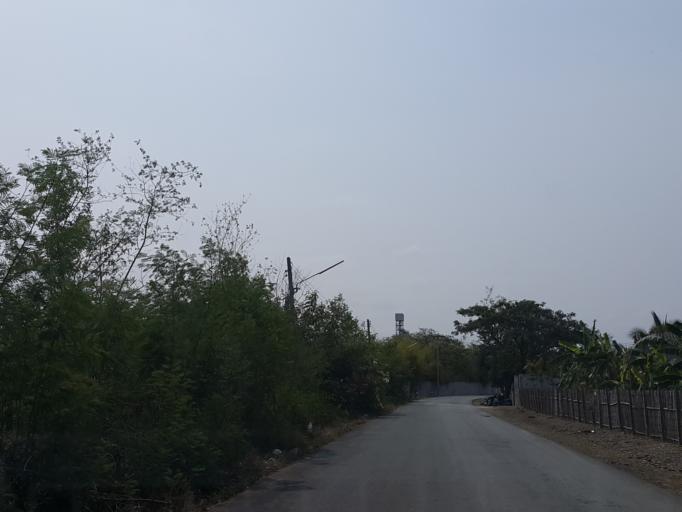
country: TH
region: Lamphun
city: Ban Thi
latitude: 18.6682
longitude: 99.0990
